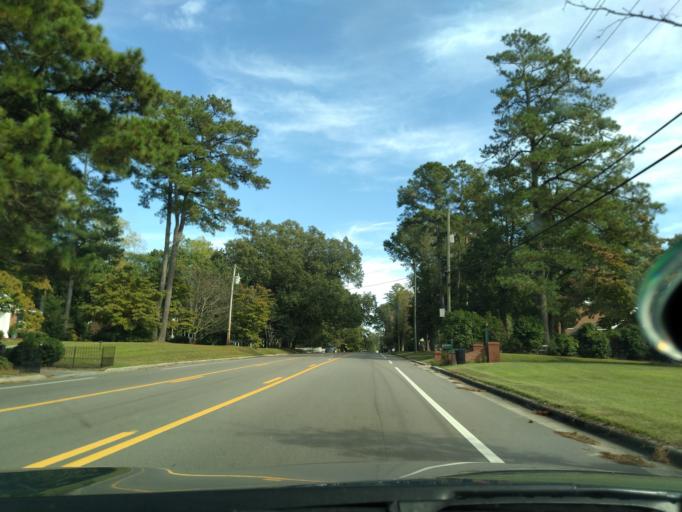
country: US
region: North Carolina
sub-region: Beaufort County
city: Washington
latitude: 35.5343
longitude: -77.0302
